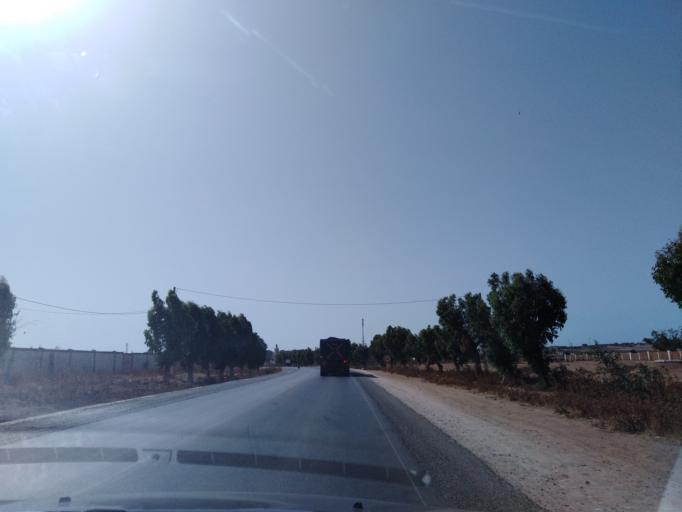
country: MA
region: Doukkala-Abda
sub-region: Safi
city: Safi
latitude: 32.2522
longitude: -8.9748
